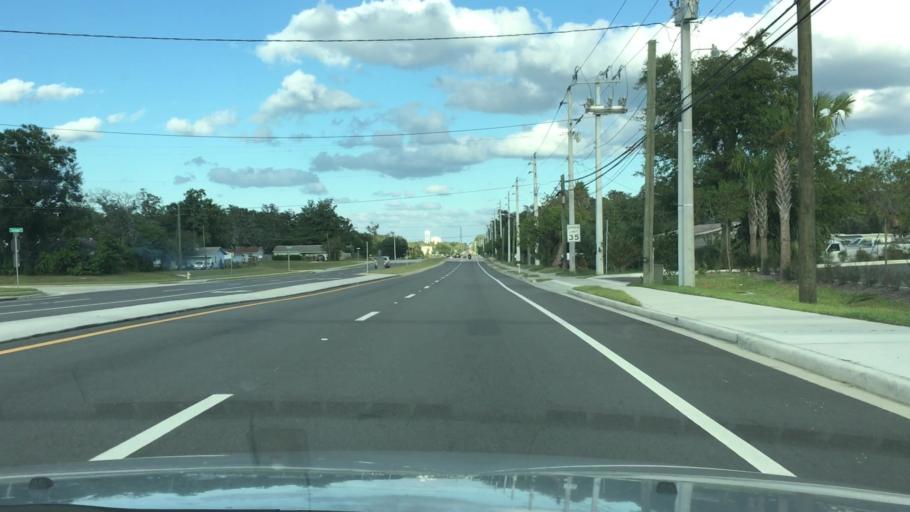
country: US
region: Florida
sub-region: Volusia County
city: Holly Hill
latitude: 29.2356
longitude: -81.0659
